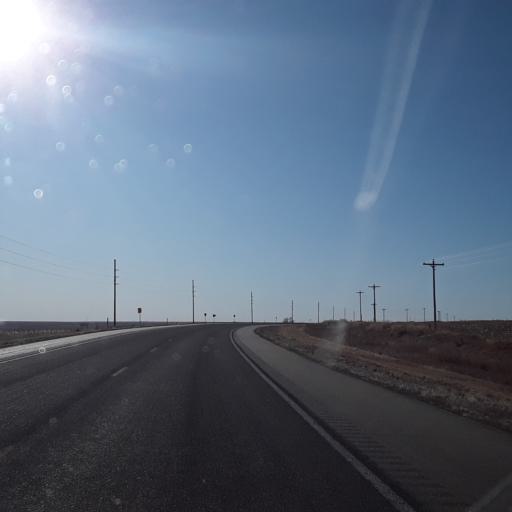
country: US
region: Nebraska
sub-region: Hitchcock County
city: Trenton
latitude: 40.1940
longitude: -100.9825
